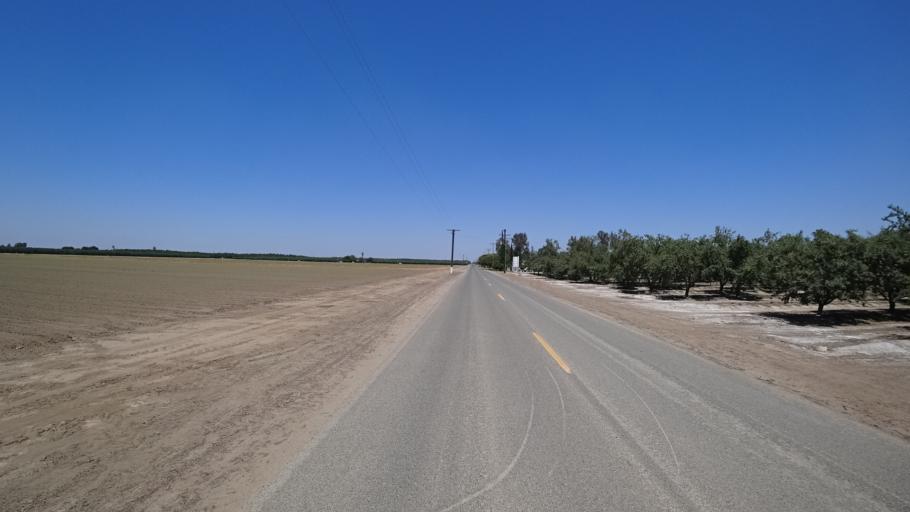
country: US
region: California
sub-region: Kings County
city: Armona
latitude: 36.3234
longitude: -119.7269
